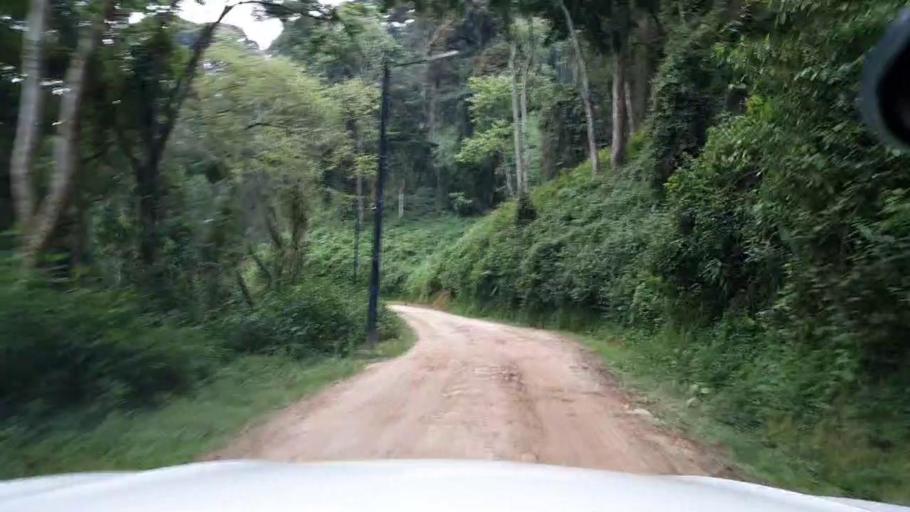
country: RW
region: Western Province
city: Cyangugu
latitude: -2.5635
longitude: 29.2281
